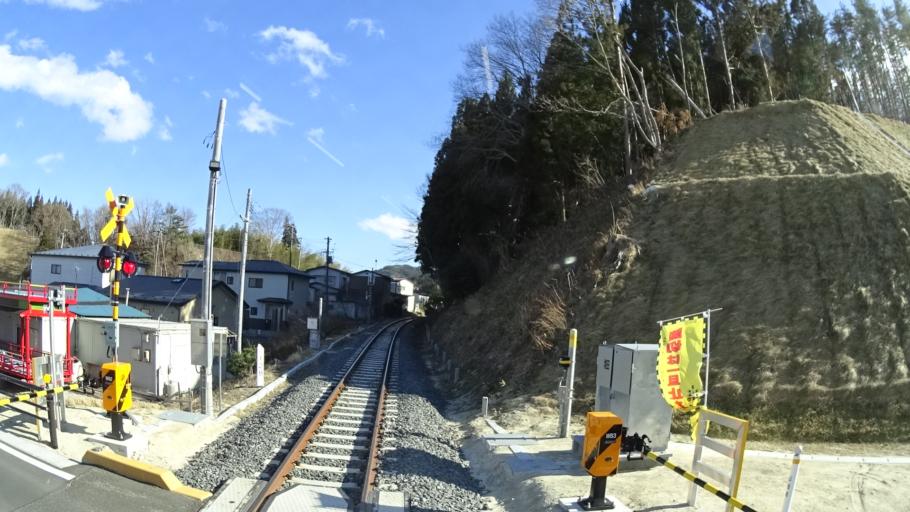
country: JP
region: Iwate
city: Yamada
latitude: 39.4596
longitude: 141.9552
